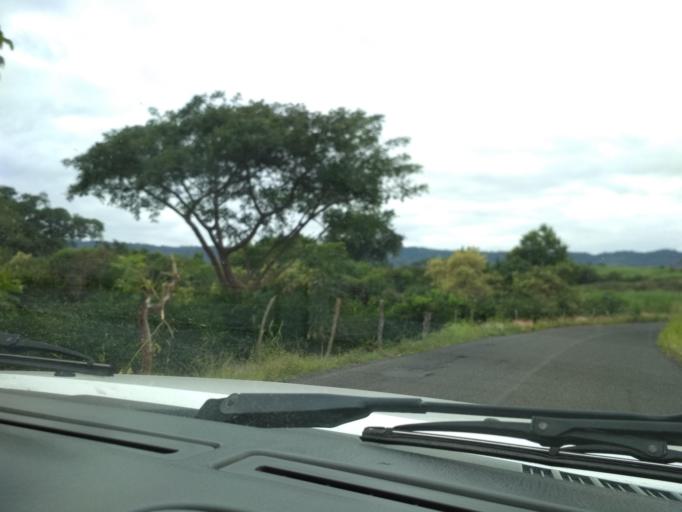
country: MX
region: Veracruz
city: El Castillo
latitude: 19.5845
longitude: -96.8100
